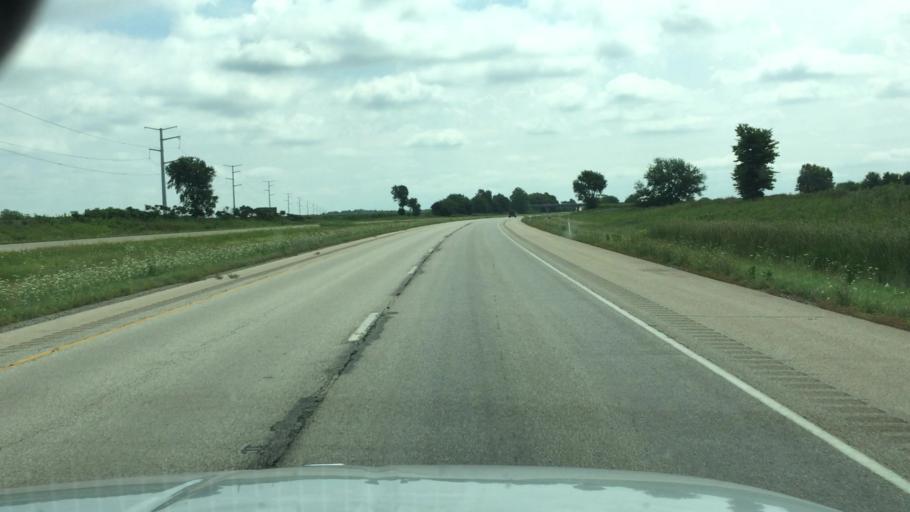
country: US
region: Illinois
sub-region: Knox County
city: Knoxville
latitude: 40.9022
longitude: -90.1652
